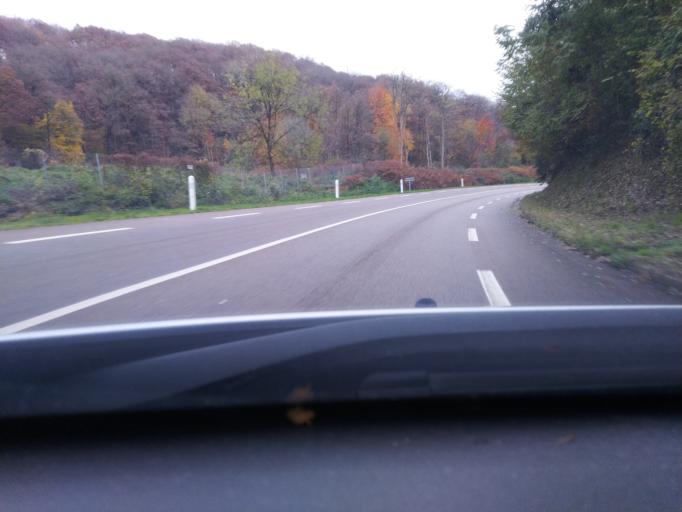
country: FR
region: Haute-Normandie
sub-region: Departement de la Seine-Maritime
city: Maromme
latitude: 49.4882
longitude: 1.0315
